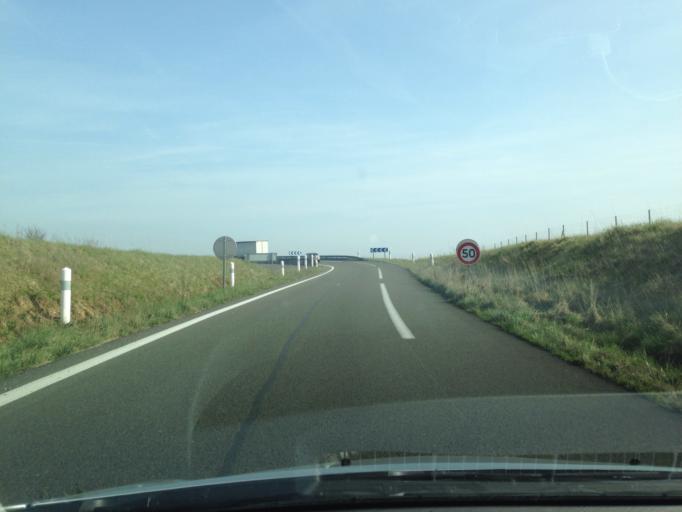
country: FR
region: Picardie
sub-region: Departement de la Somme
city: Abbeville
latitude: 50.1310
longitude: 1.8122
